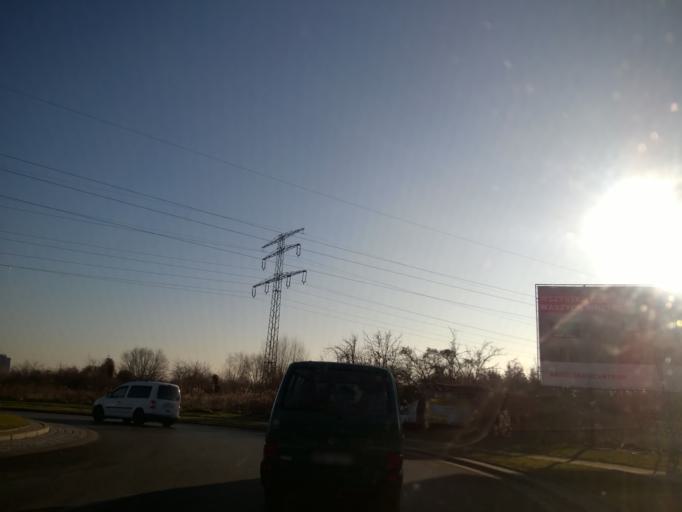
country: PL
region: Lower Silesian Voivodeship
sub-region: Powiat wroclawski
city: Wroclaw
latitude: 51.1182
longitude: 16.9821
